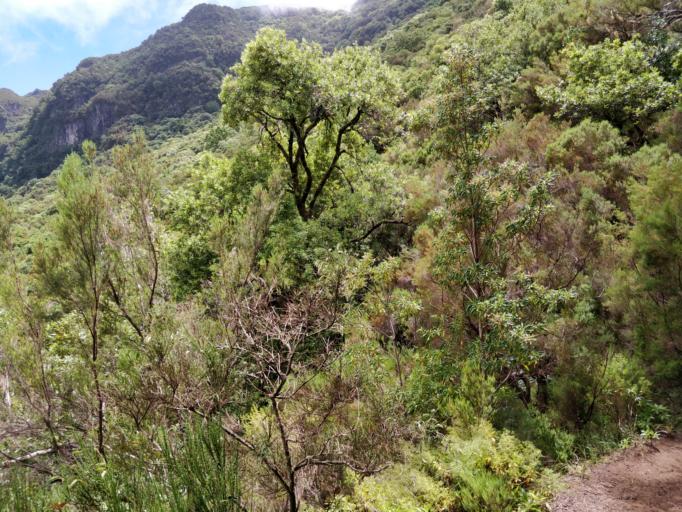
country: PT
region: Madeira
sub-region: Calheta
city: Arco da Calheta
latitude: 32.7635
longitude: -17.1312
